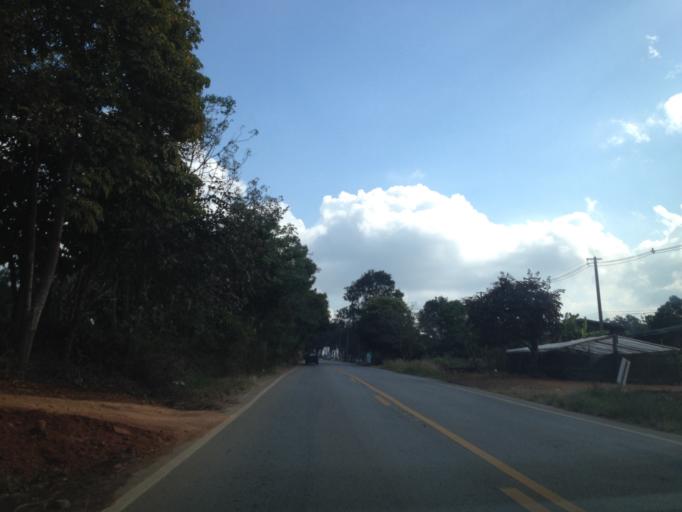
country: TH
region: Chiang Mai
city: Hot
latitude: 18.1466
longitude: 98.3450
